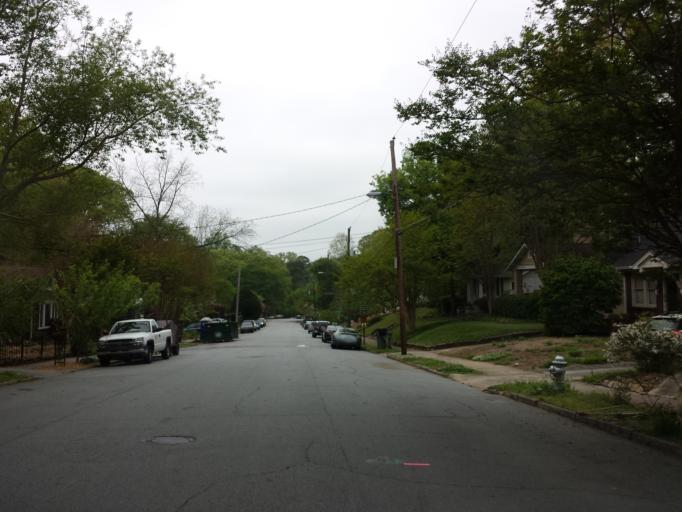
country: US
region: Georgia
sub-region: DeKalb County
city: Druid Hills
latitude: 33.7900
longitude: -84.3570
